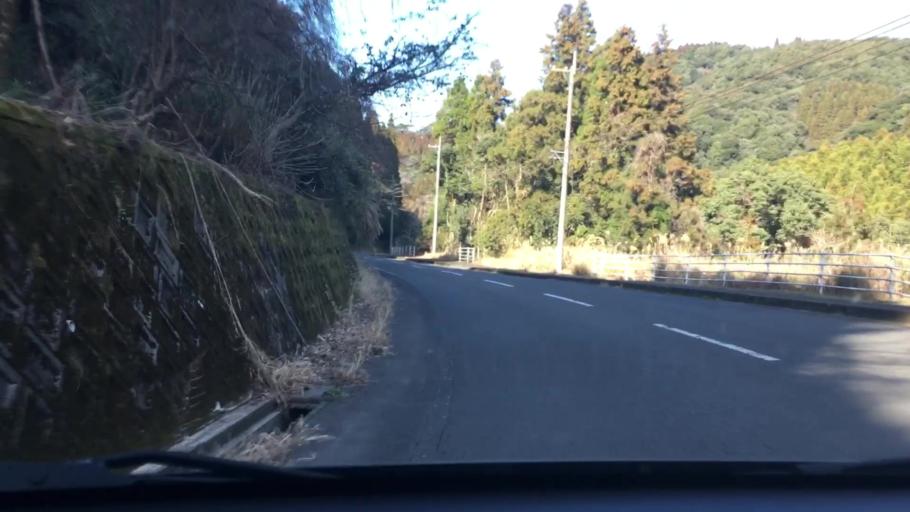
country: JP
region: Kagoshima
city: Satsumasendai
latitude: 31.7528
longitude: 130.4109
